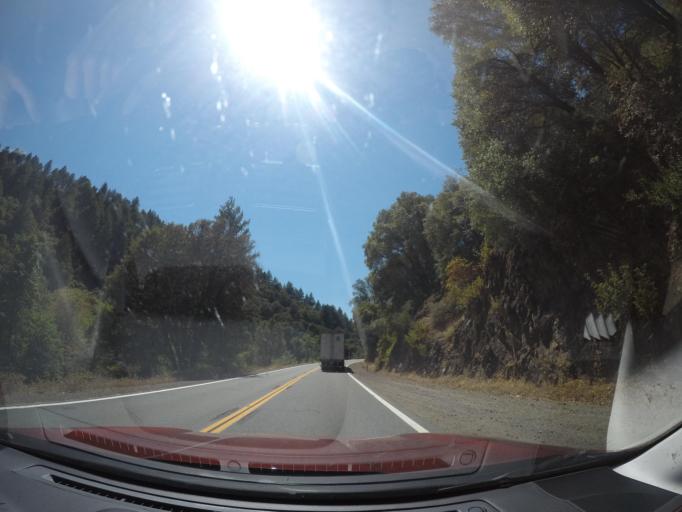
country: US
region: California
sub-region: Shasta County
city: Bella Vista
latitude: 40.7463
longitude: -122.0566
